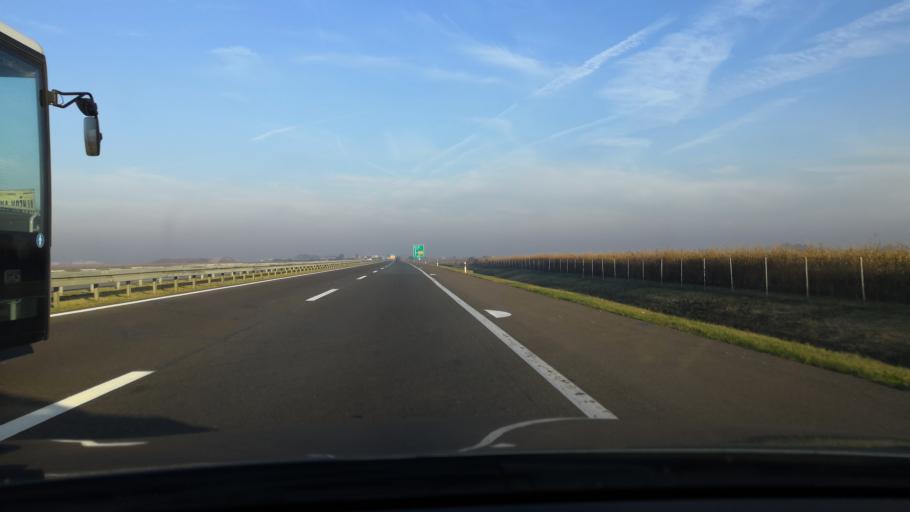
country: RS
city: Novi Karlovci
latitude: 45.0594
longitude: 20.1649
